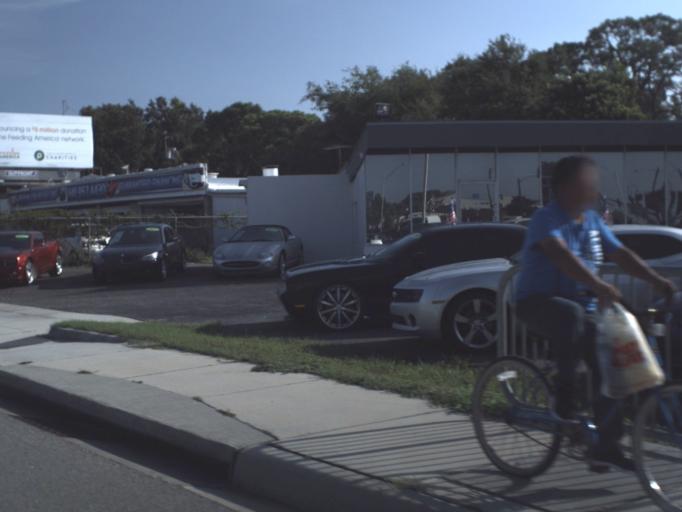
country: US
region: Florida
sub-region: Sarasota County
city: Sarasota
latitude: 27.3538
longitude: -82.5303
